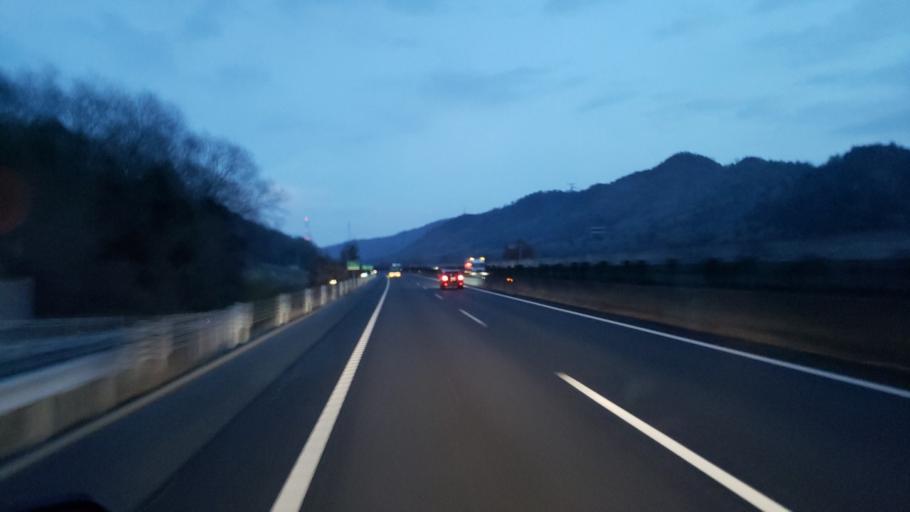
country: JP
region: Hyogo
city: Kakogawacho-honmachi
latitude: 34.8514
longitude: 134.7908
